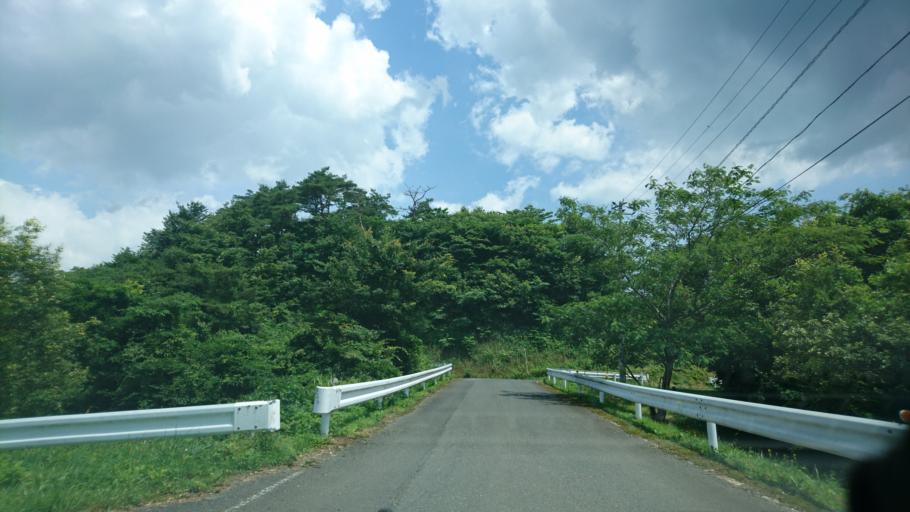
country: JP
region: Iwate
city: Ichinoseki
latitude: 38.9185
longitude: 141.2166
